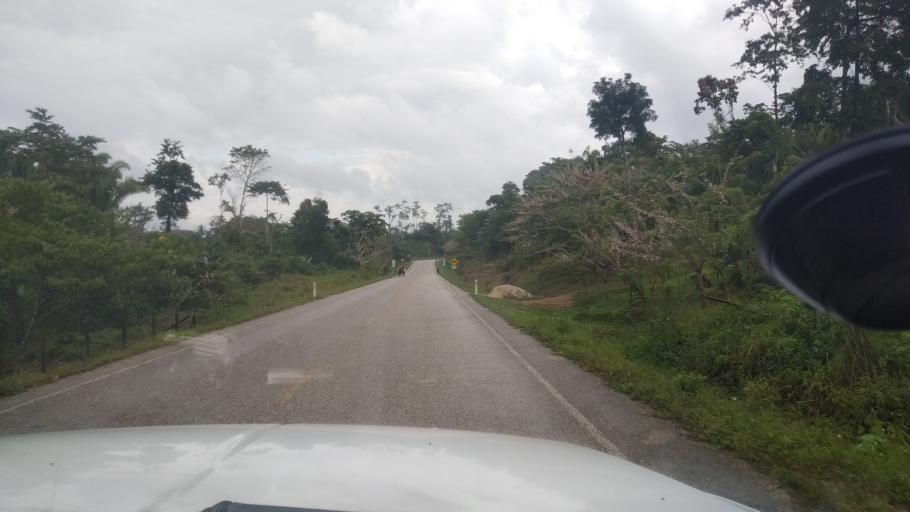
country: GT
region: Peten
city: San Luis
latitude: 16.2003
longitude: -89.1486
